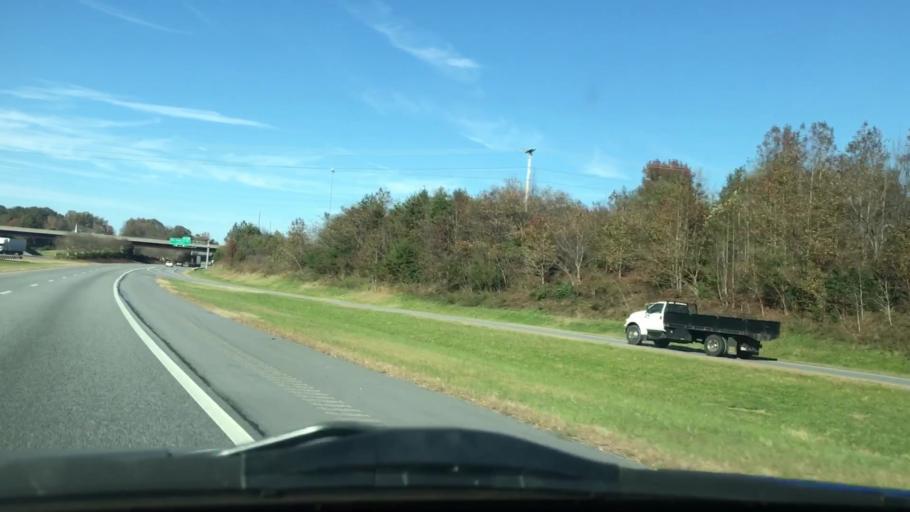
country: US
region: North Carolina
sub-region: Guilford County
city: High Point
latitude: 35.9520
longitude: -79.9753
